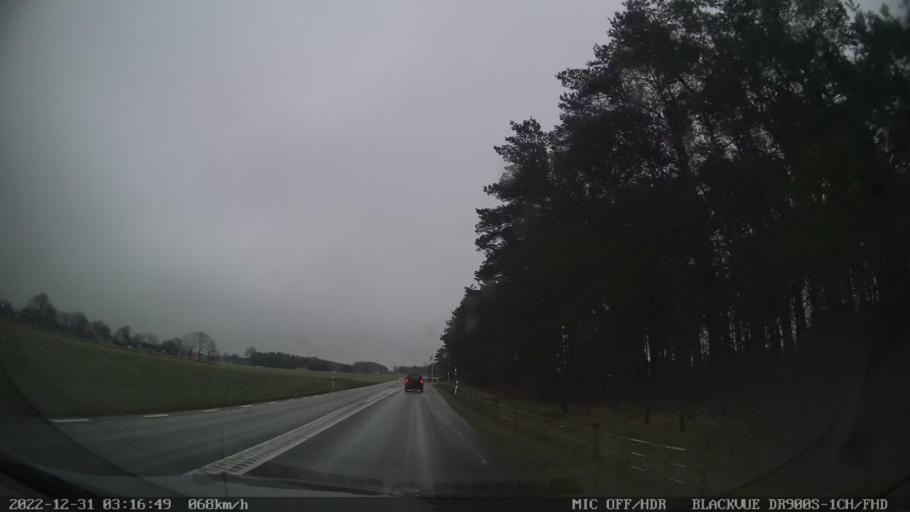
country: SE
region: Skane
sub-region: Tomelilla Kommun
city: Tomelilla
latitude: 55.5523
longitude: 14.0771
